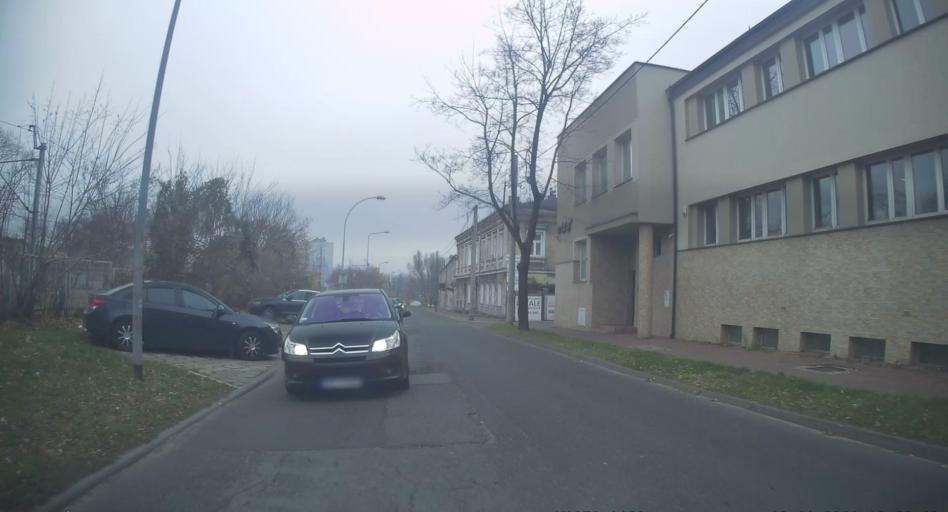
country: PL
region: Silesian Voivodeship
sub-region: Czestochowa
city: Czestochowa
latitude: 50.8151
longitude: 19.1220
